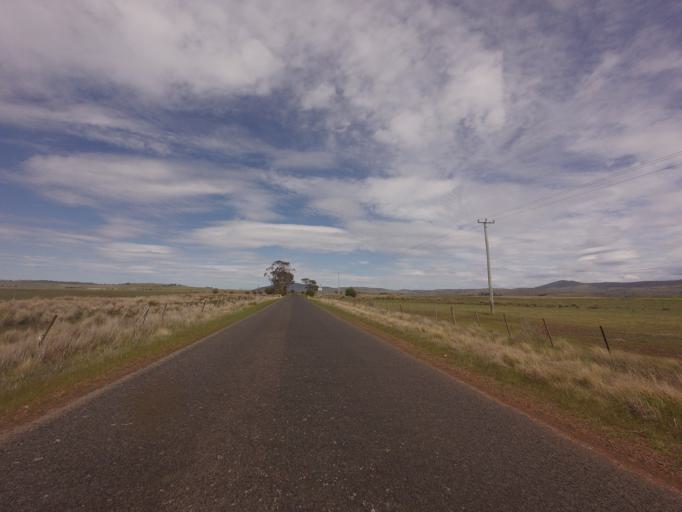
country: AU
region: Tasmania
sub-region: Northern Midlands
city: Evandale
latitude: -41.8656
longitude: 147.3492
